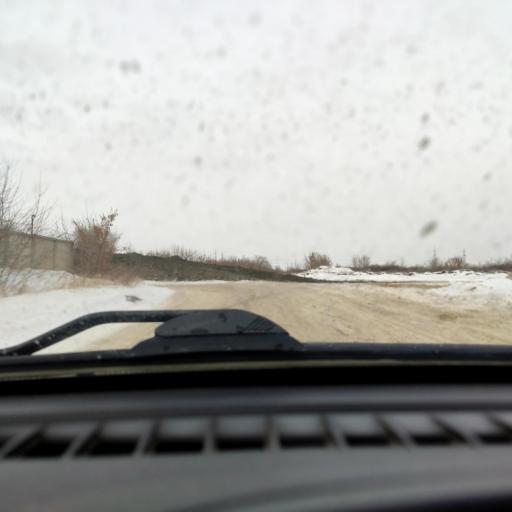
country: RU
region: Samara
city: Tol'yatti
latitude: 53.5856
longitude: 49.2655
